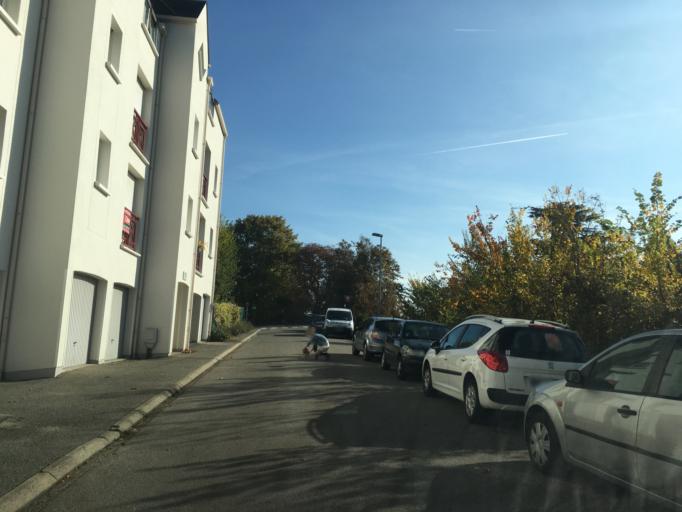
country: FR
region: Haute-Normandie
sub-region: Departement de l'Eure
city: Vernon
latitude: 49.0880
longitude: 1.4886
